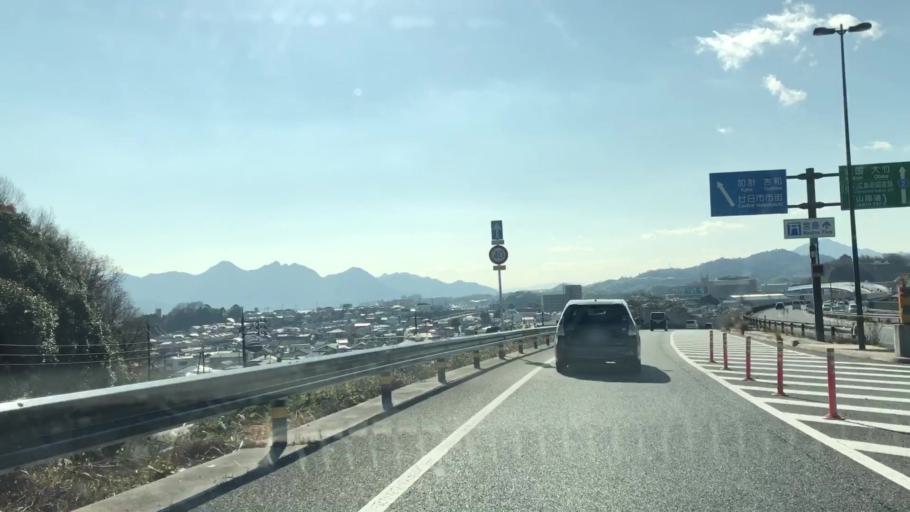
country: JP
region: Hiroshima
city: Hatsukaichi
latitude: 34.3602
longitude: 132.3289
